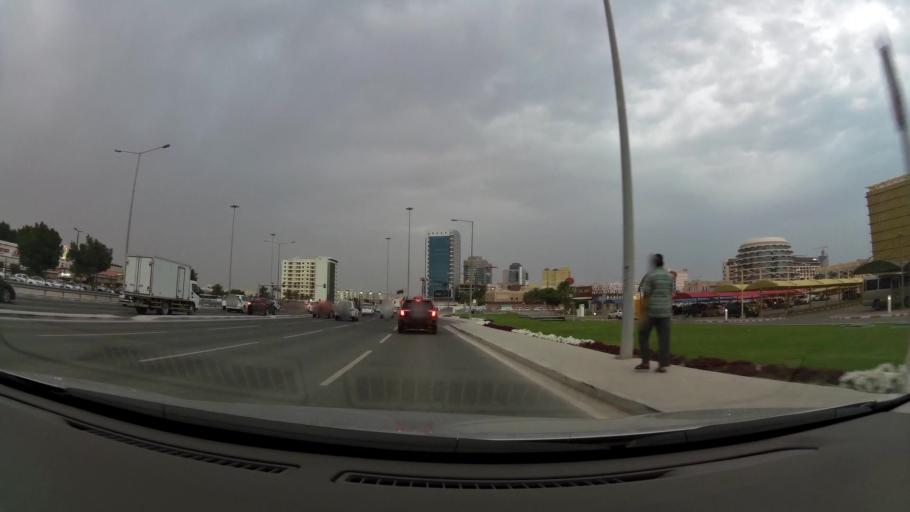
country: QA
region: Baladiyat ad Dawhah
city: Doha
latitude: 25.2715
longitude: 51.5119
